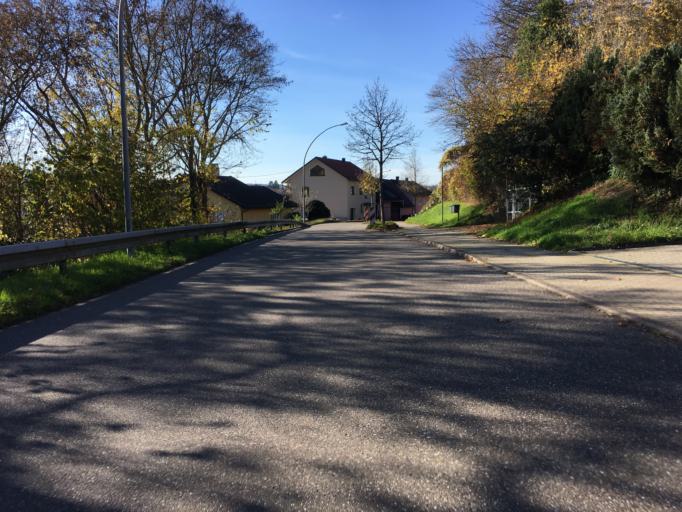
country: DE
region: Baden-Wuerttemberg
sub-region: Karlsruhe Region
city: Oberderdingen
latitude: 49.0891
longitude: 8.7902
